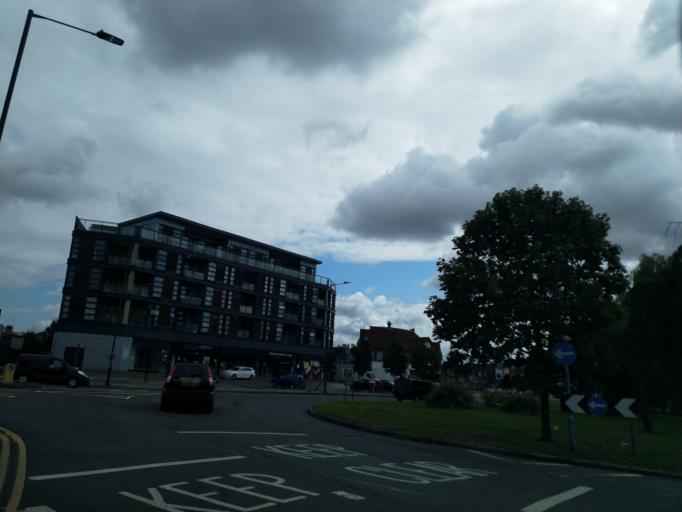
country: GB
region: England
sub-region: Greater London
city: Edgware
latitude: 51.5851
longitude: -0.2823
